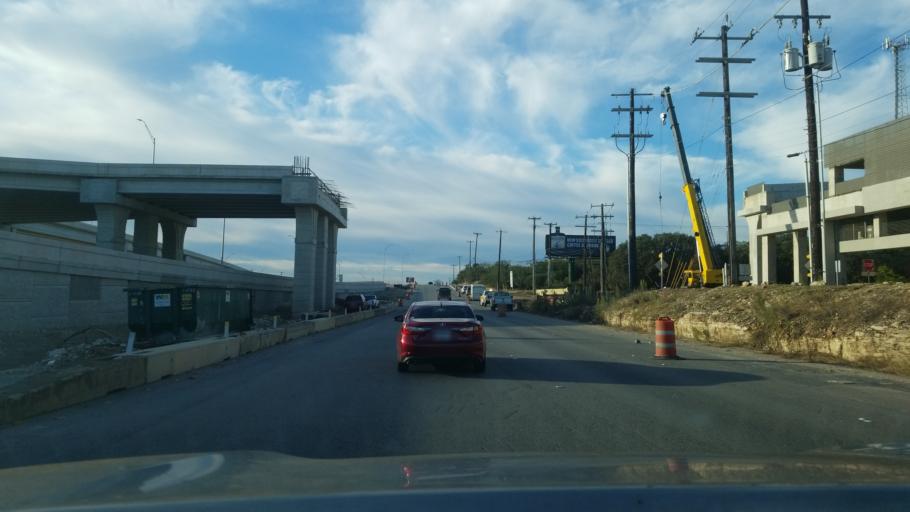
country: US
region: Texas
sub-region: Bexar County
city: Hollywood Park
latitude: 29.6476
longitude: -98.4518
